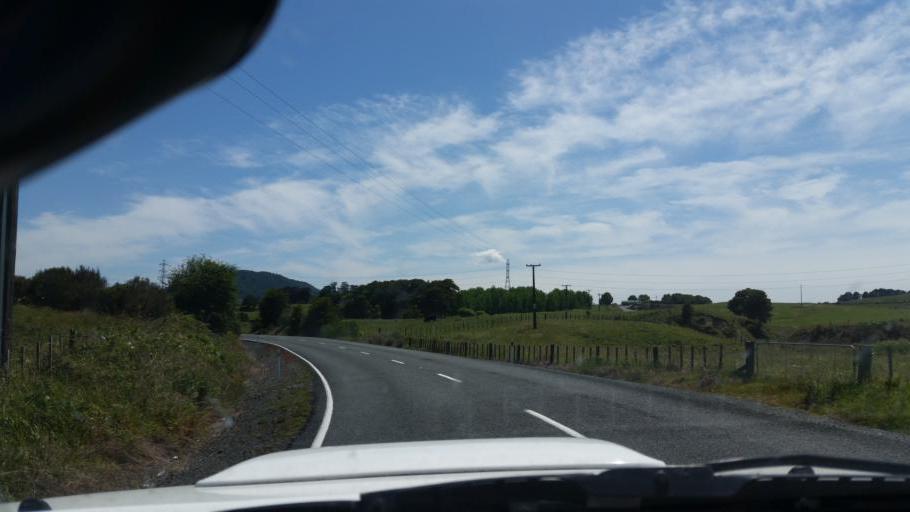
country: NZ
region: Auckland
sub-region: Auckland
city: Wellsford
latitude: -36.1688
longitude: 174.4223
